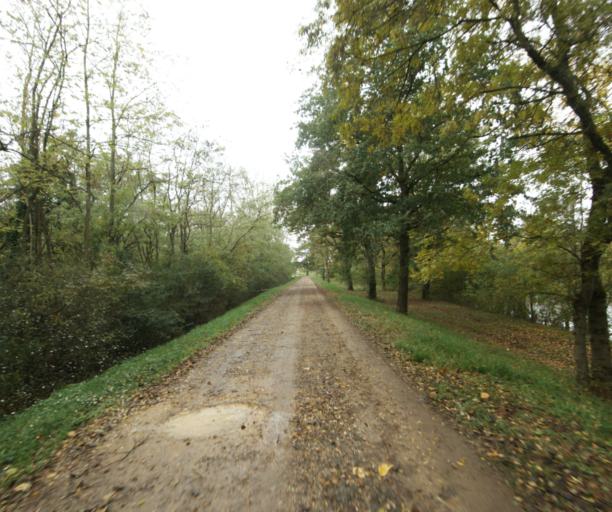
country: FR
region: Rhone-Alpes
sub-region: Departement de l'Ain
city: Pont-de-Vaux
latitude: 46.4561
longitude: 4.8975
